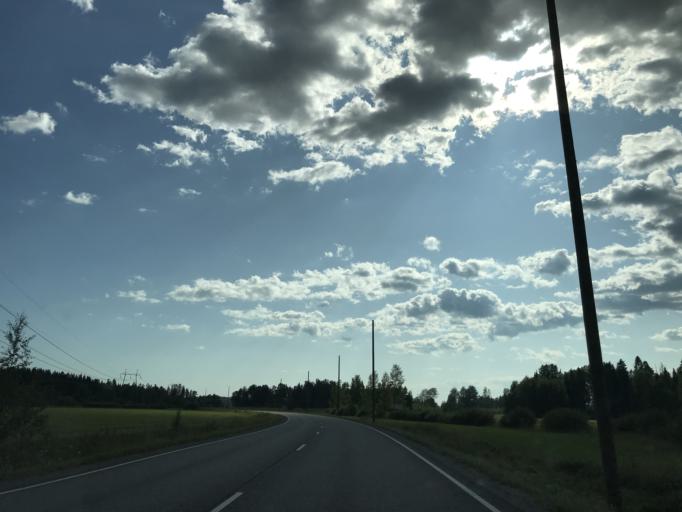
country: FI
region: Uusimaa
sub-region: Helsinki
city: Nurmijaervi
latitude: 60.4547
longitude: 24.7066
